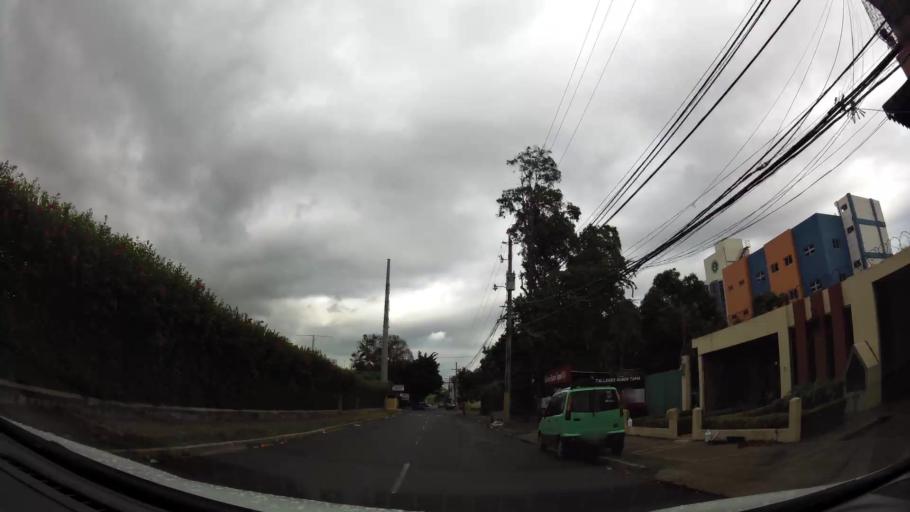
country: DO
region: Nacional
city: La Agustina
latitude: 18.4871
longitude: -69.9312
